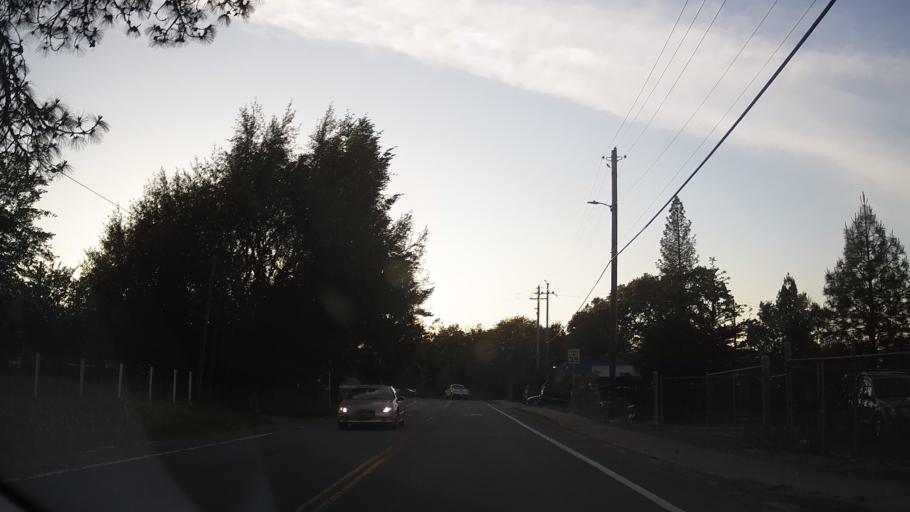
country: US
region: California
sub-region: Mendocino County
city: Willits
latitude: 39.3969
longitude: -123.3457
